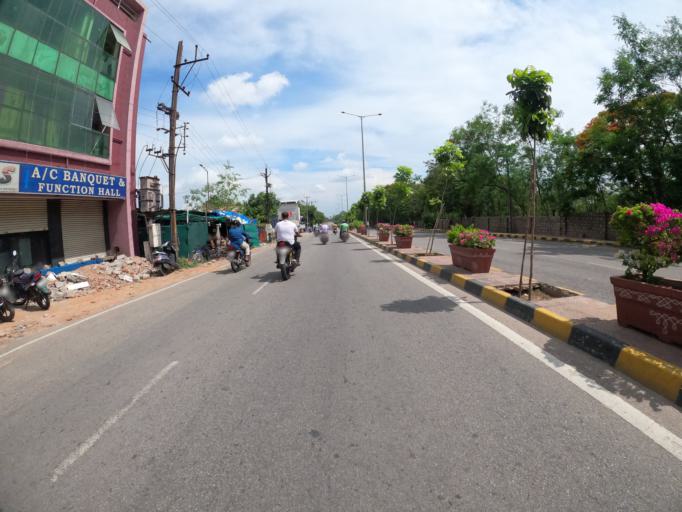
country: IN
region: Telangana
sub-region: Hyderabad
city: Hyderabad
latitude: 17.3899
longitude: 78.4229
